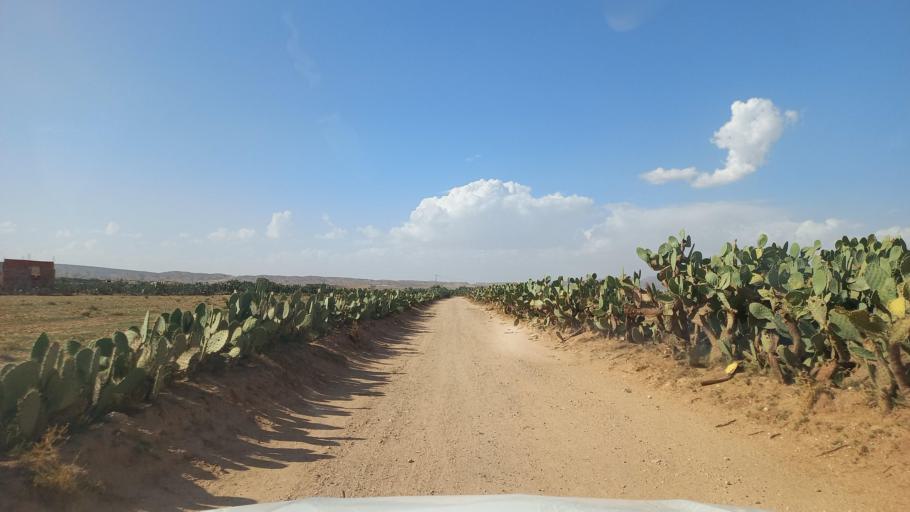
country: TN
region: Al Qasrayn
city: Sbiba
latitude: 35.3147
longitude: 9.0305
